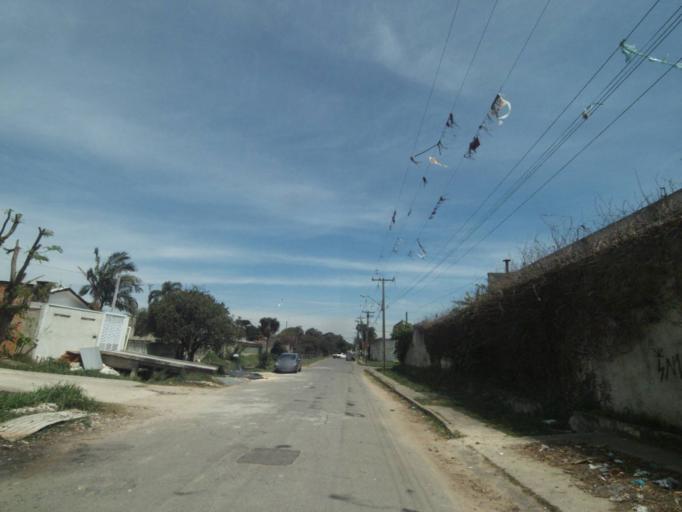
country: BR
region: Parana
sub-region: Sao Jose Dos Pinhais
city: Sao Jose dos Pinhais
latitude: -25.4978
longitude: -49.2240
